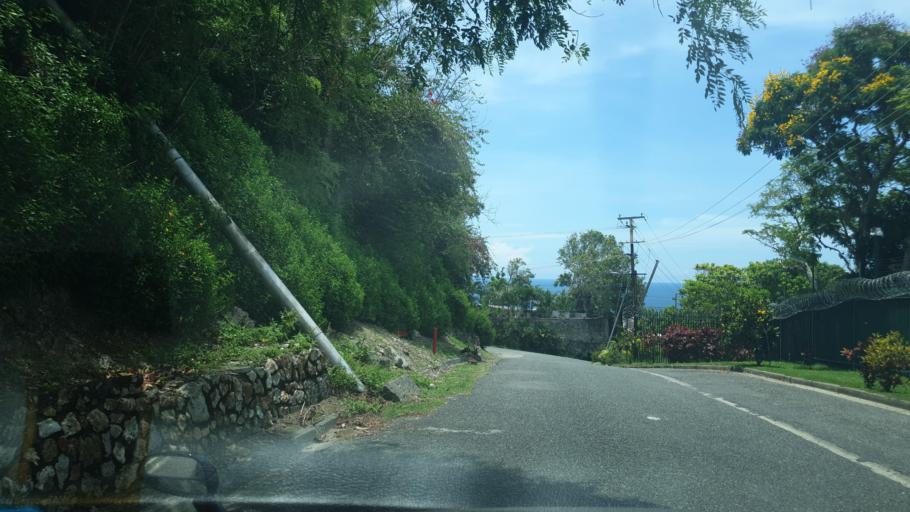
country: PG
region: National Capital
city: Port Moresby
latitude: -9.4740
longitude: 147.1568
